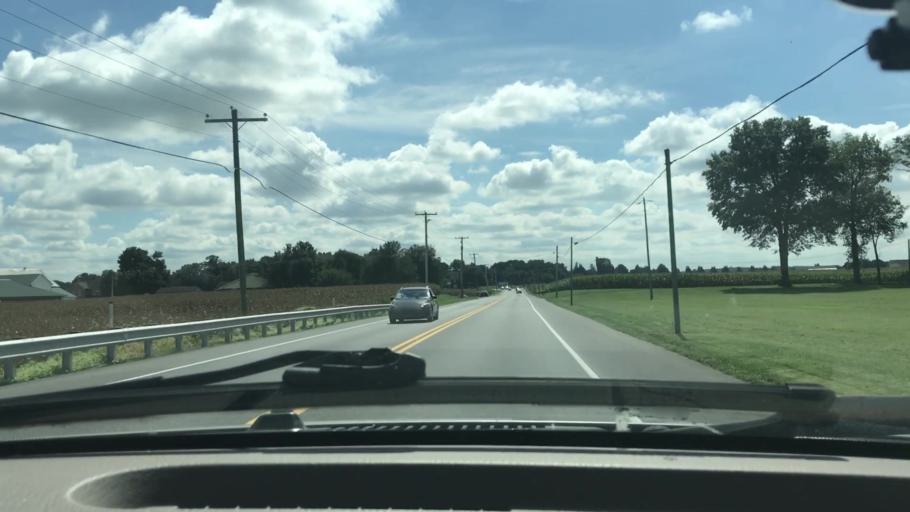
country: US
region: Pennsylvania
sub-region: Lancaster County
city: Manheim
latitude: 40.1305
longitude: -76.3803
